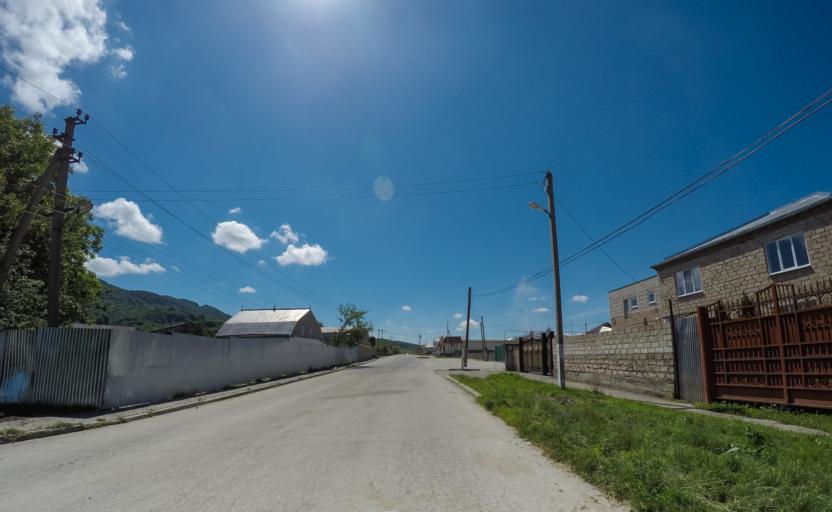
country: RU
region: Kabardino-Balkariya
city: Belaya Rechka
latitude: 43.4249
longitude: 43.5797
